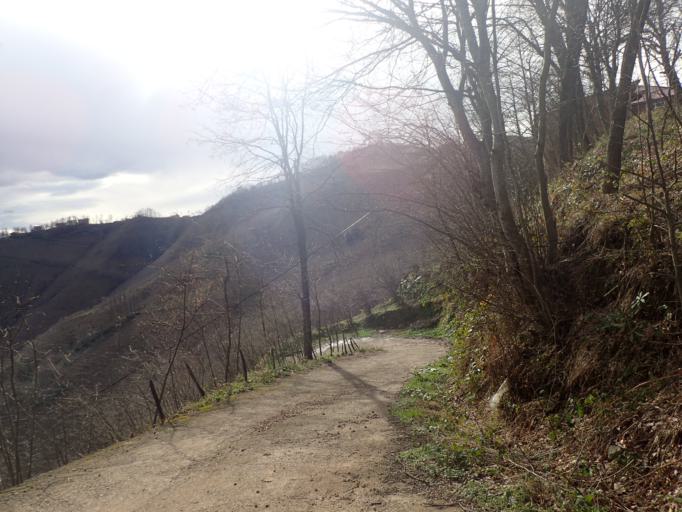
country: TR
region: Ordu
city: Camas
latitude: 40.8855
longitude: 37.5810
